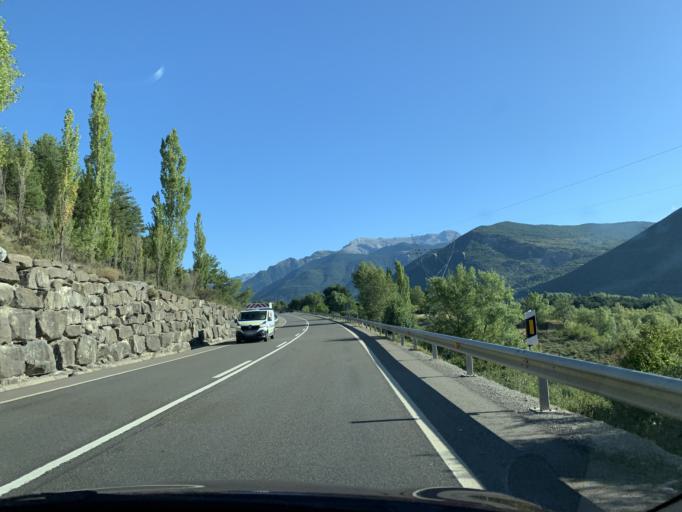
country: ES
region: Aragon
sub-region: Provincia de Huesca
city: Biescas
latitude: 42.5741
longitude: -0.3245
